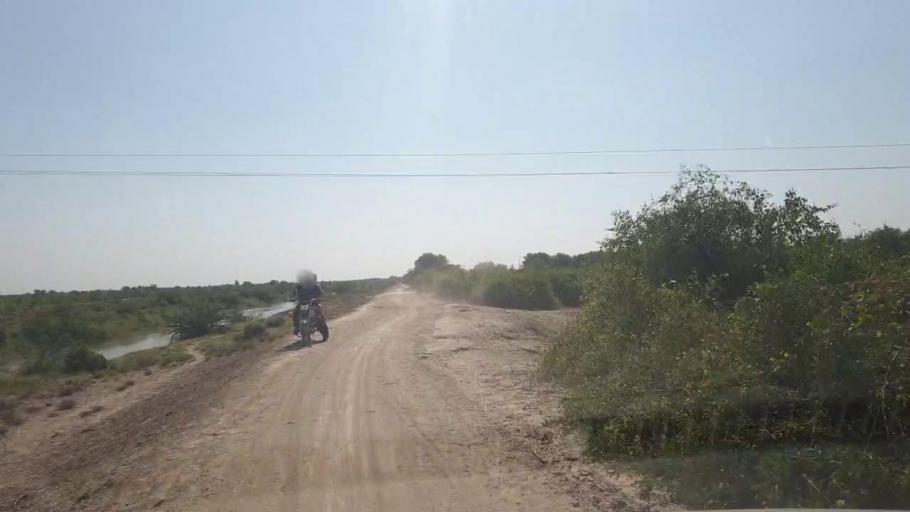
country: PK
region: Sindh
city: Tando Bago
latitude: 24.9180
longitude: 69.1645
